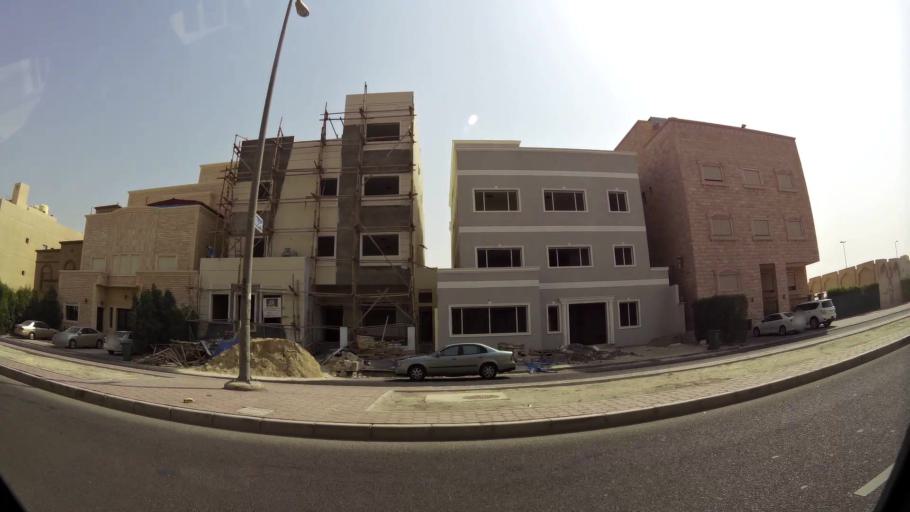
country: KW
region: Muhafazat al Jahra'
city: Al Jahra'
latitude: 29.3207
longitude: 47.7379
